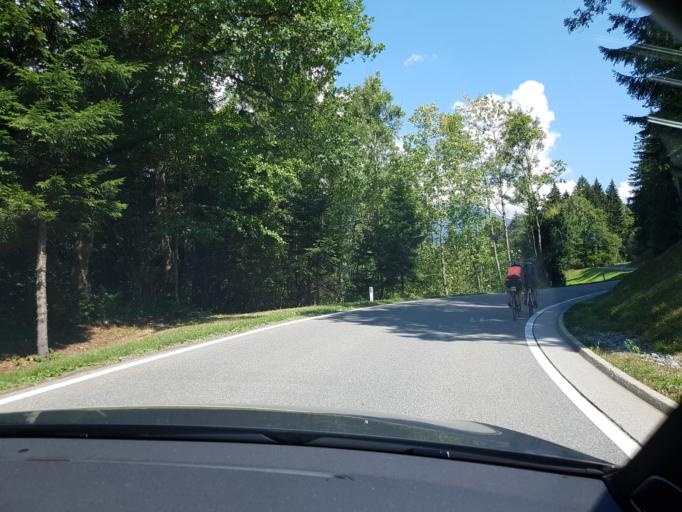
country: AT
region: Vorarlberg
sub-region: Politischer Bezirk Bludenz
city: Ludesch
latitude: 47.2045
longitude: 9.7922
